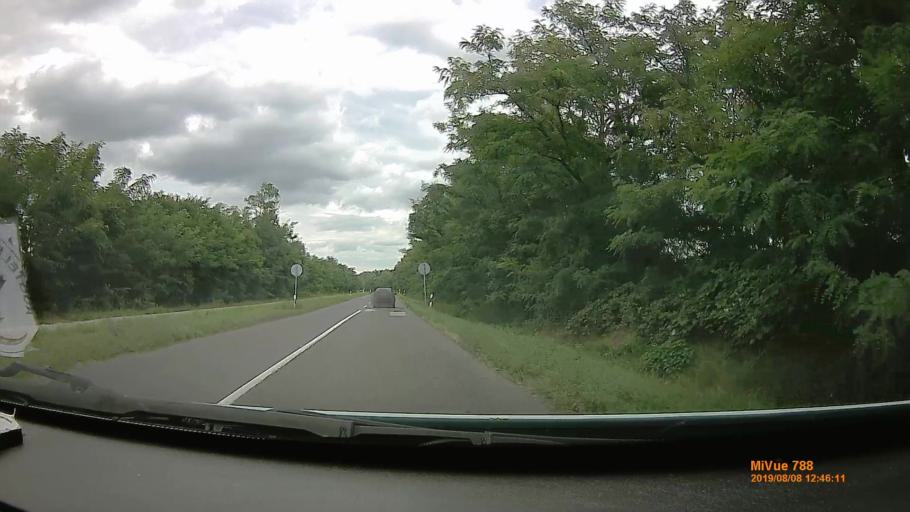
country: HU
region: Szabolcs-Szatmar-Bereg
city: Hodasz
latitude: 47.8946
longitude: 22.2160
